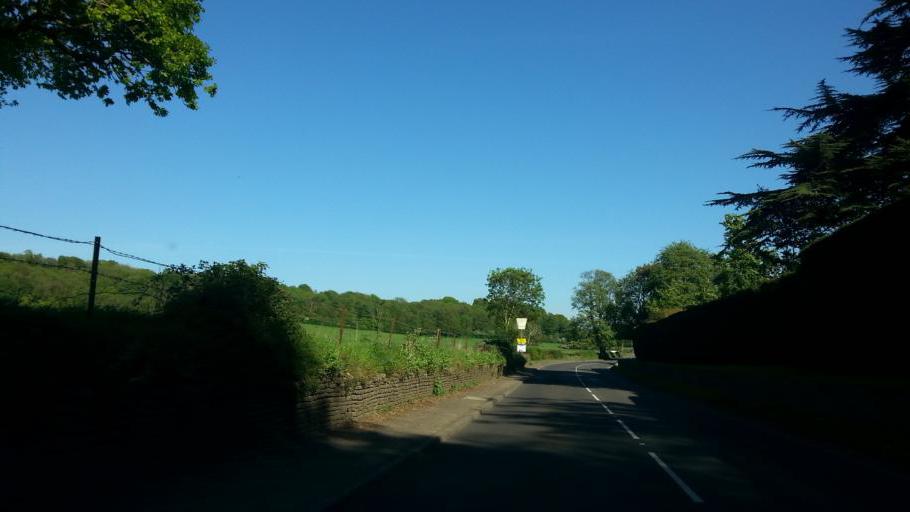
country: GB
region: England
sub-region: Somerset
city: Milborne Port
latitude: 50.9656
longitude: -2.4567
